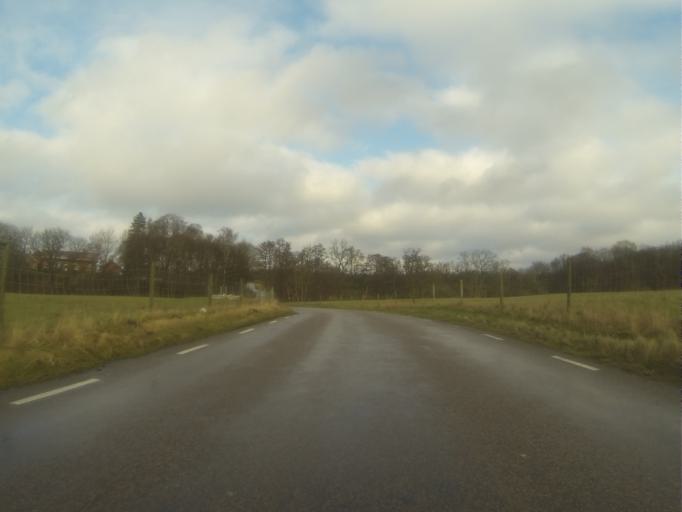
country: SE
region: Skane
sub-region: Svedala Kommun
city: Klagerup
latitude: 55.5566
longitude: 13.3159
